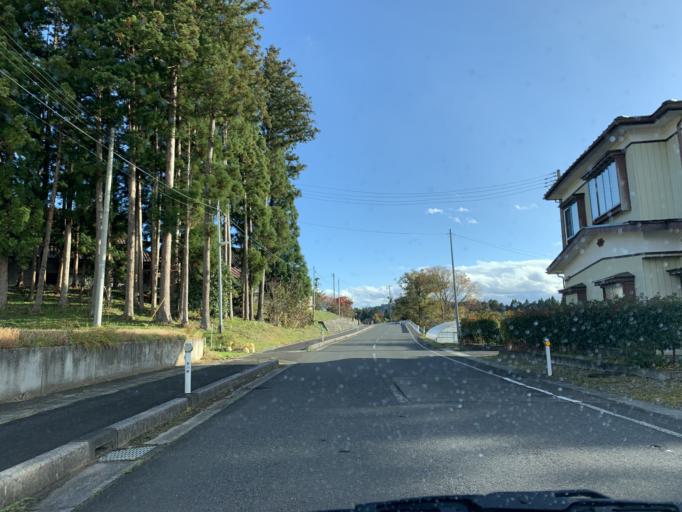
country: JP
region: Iwate
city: Ichinoseki
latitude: 39.0200
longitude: 141.0875
